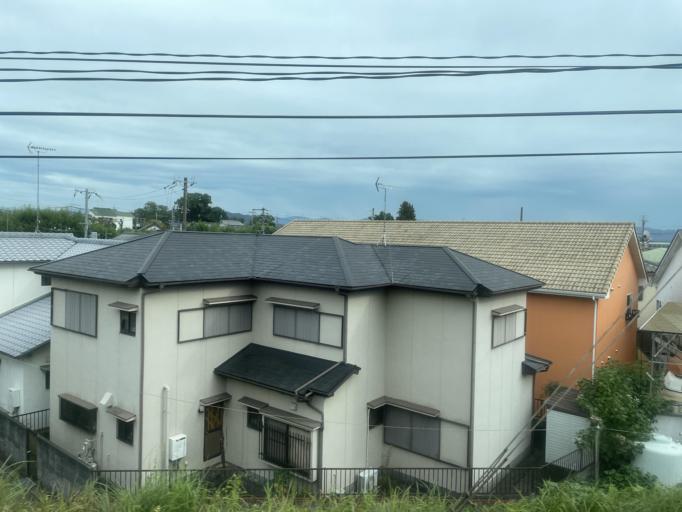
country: JP
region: Wakayama
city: Wakayama-shi
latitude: 34.2654
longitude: 135.2098
